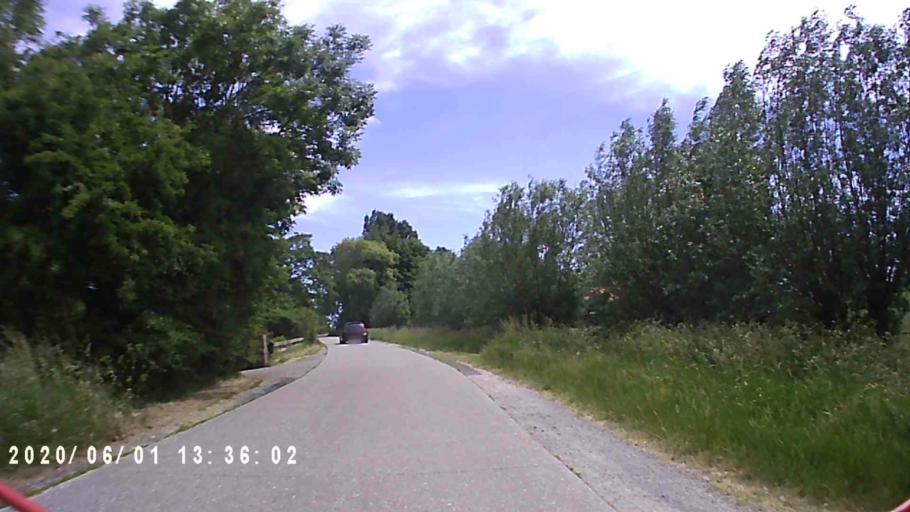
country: NL
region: Friesland
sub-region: Gemeente Littenseradiel
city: Wommels
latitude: 53.0872
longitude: 5.5854
